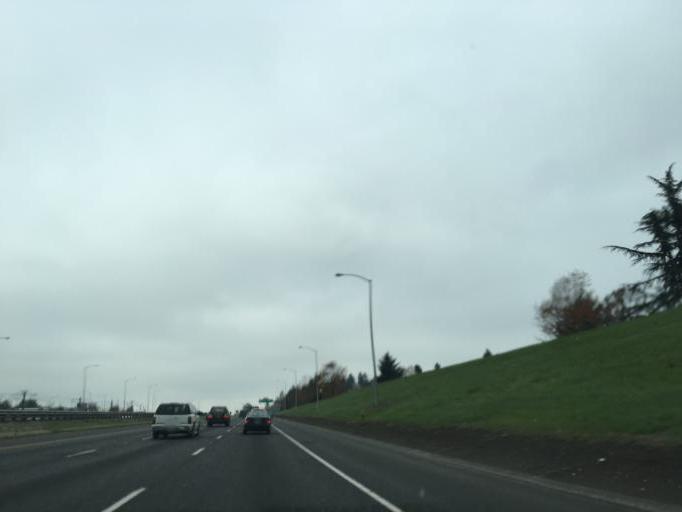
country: US
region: Oregon
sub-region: Multnomah County
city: Lents
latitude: 45.4911
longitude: -122.5656
